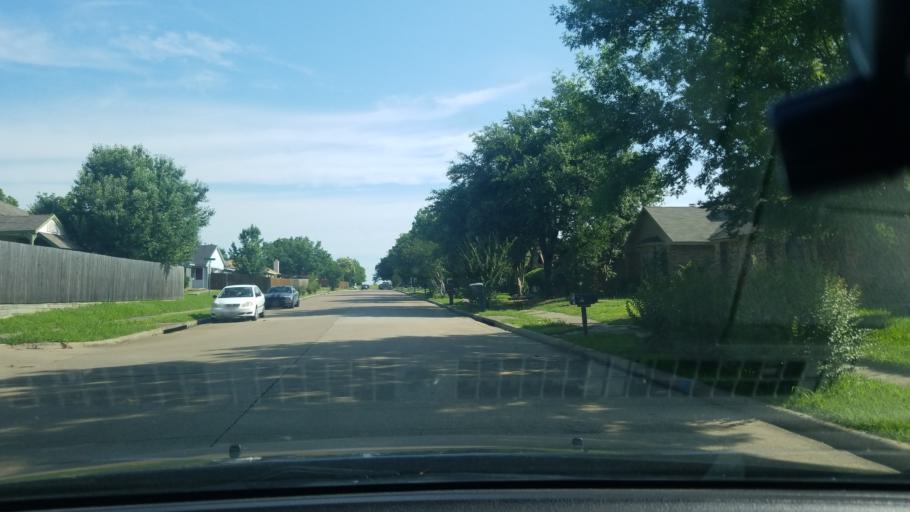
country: US
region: Texas
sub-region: Dallas County
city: Sunnyvale
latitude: 32.7765
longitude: -96.5710
